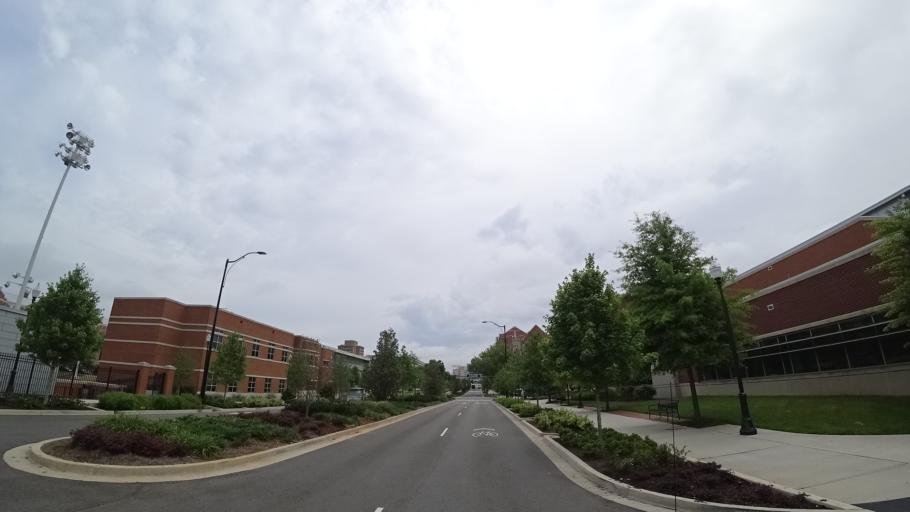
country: US
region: Tennessee
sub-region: Knox County
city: Knoxville
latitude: 35.9505
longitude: -83.9314
